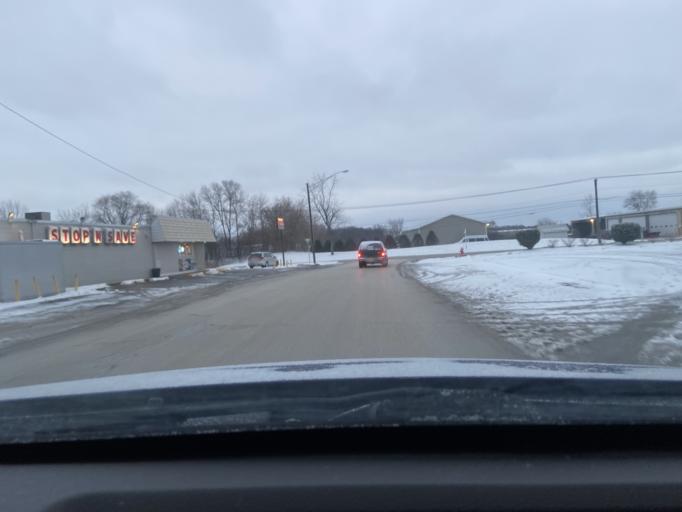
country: US
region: Illinois
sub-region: Lake County
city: Round Lake Park
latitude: 42.3487
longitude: -88.0768
